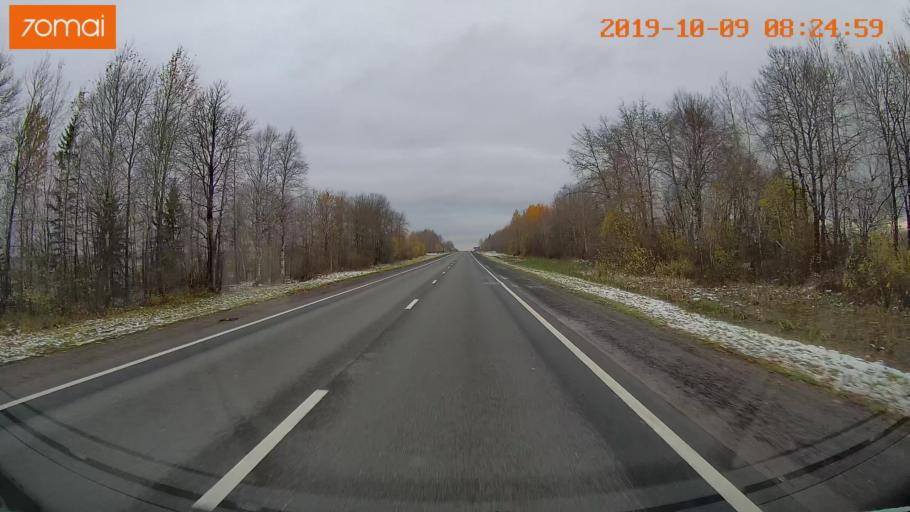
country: RU
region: Vologda
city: Gryazovets
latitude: 58.7741
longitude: 40.2752
